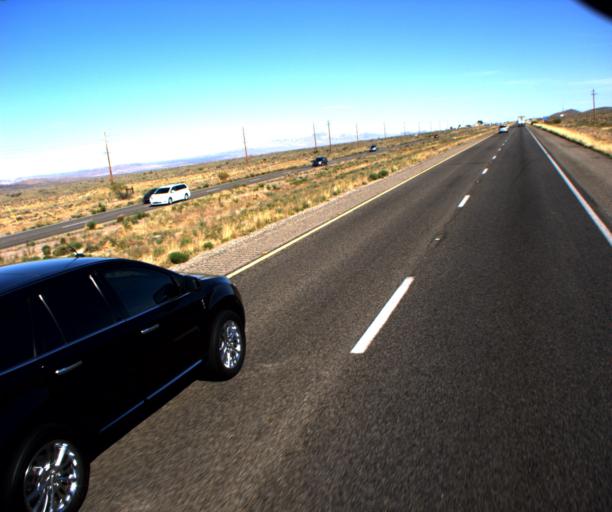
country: US
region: Arizona
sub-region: Mohave County
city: Golden Valley
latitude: 35.3888
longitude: -114.2533
